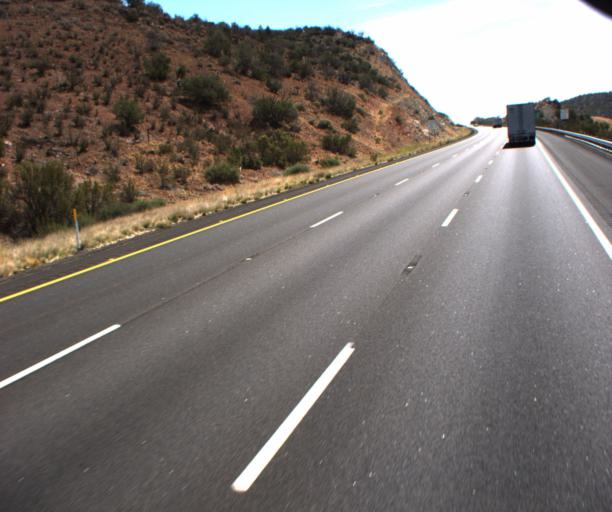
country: US
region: Arizona
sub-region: Mohave County
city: Peach Springs
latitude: 35.1881
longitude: -113.4194
